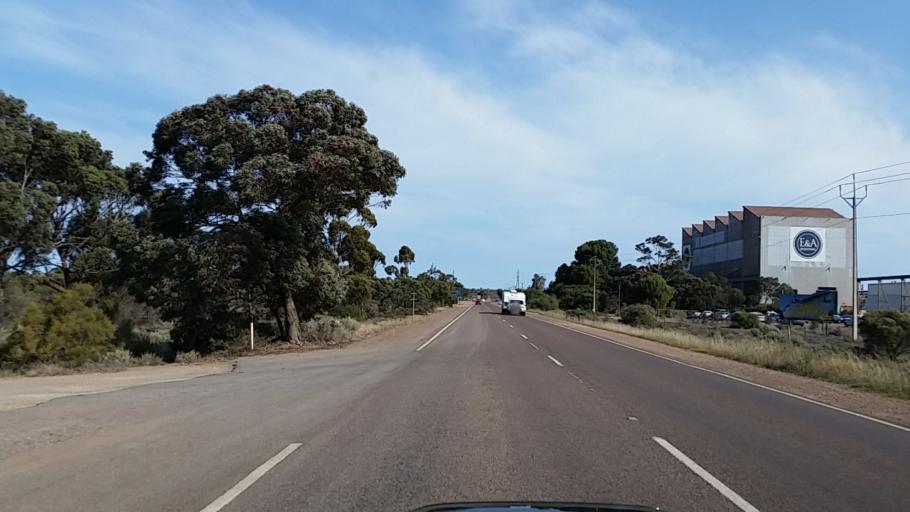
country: AU
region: South Australia
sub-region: Whyalla
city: Whyalla
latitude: -33.0032
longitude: 137.5765
